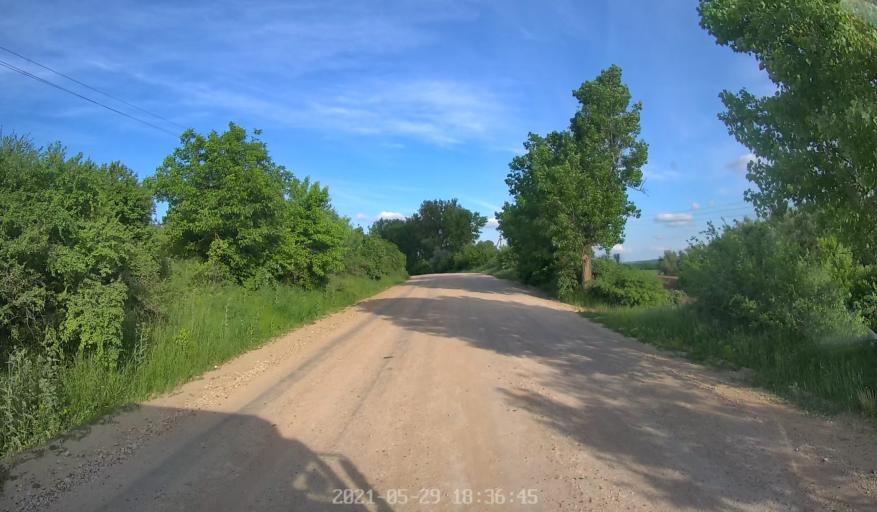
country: MD
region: Chisinau
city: Singera
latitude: 46.8057
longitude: 28.9264
